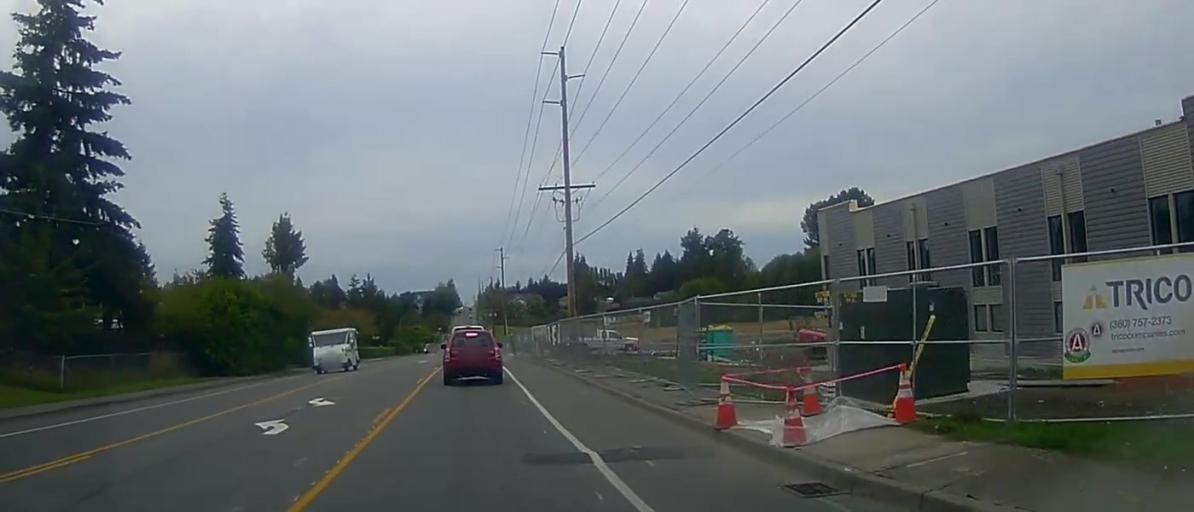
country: US
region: Washington
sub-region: Skagit County
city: Mount Vernon
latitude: 48.4429
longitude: -122.3157
